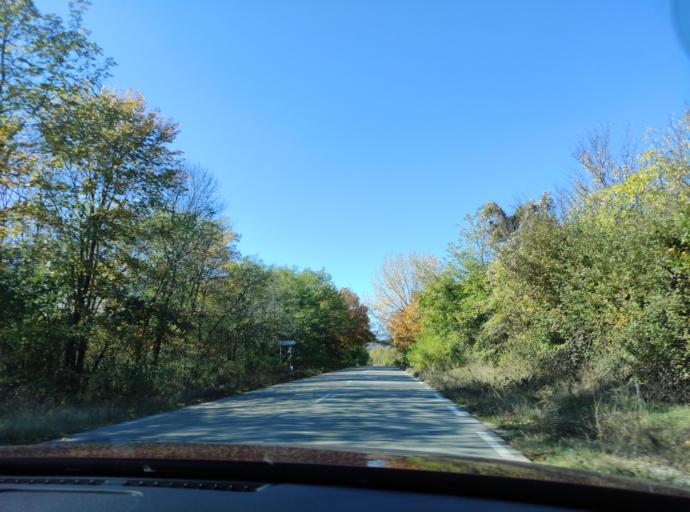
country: BG
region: Montana
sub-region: Obshtina Chiprovtsi
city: Chiprovtsi
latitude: 43.4277
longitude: 23.0031
